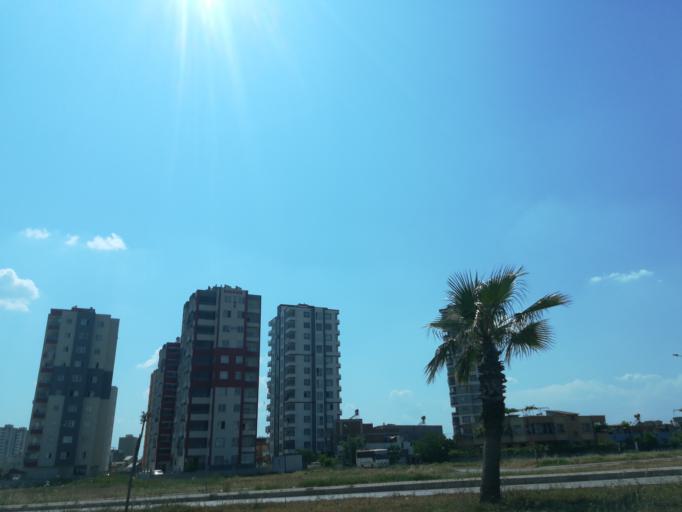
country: TR
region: Adana
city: Yuregir
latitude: 37.0152
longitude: 35.3996
